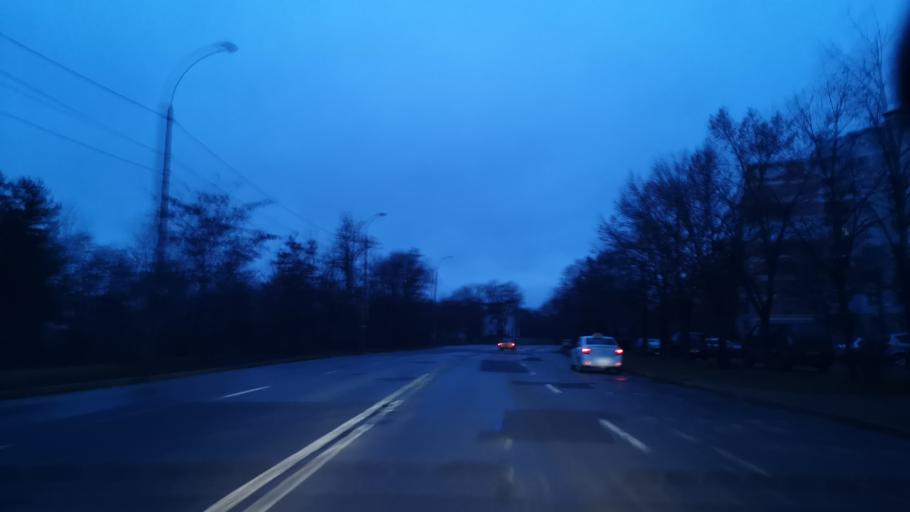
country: MD
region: Chisinau
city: Chisinau
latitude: 47.0329
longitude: 28.8784
